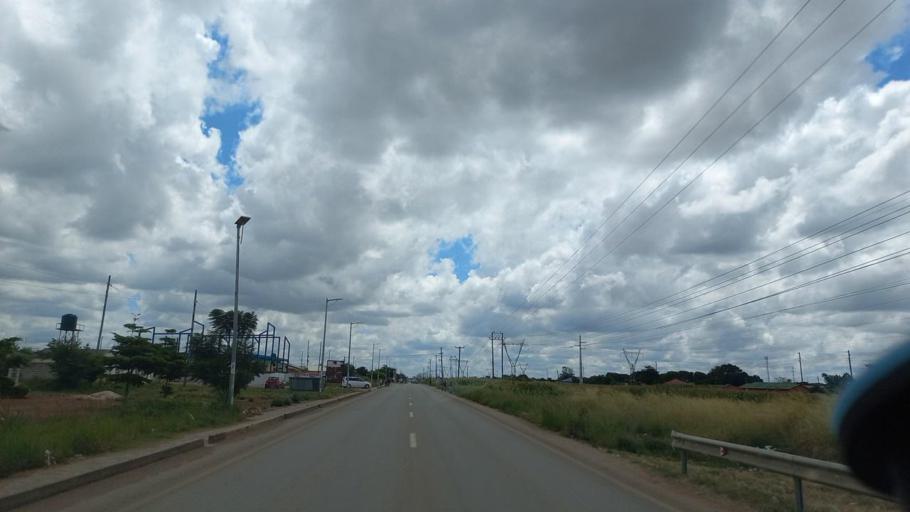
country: ZM
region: Lusaka
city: Lusaka
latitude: -15.4607
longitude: 28.3373
